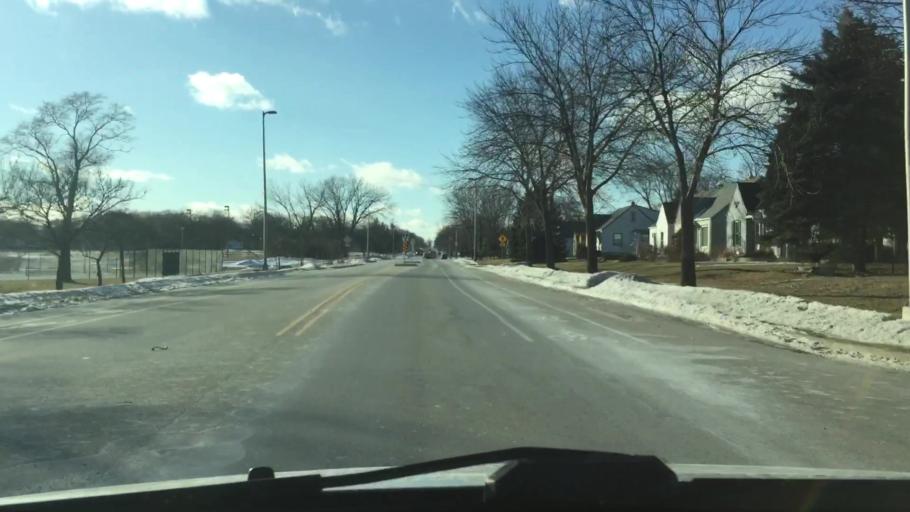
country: US
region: Wisconsin
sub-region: Milwaukee County
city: West Milwaukee
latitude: 42.9740
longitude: -87.9597
